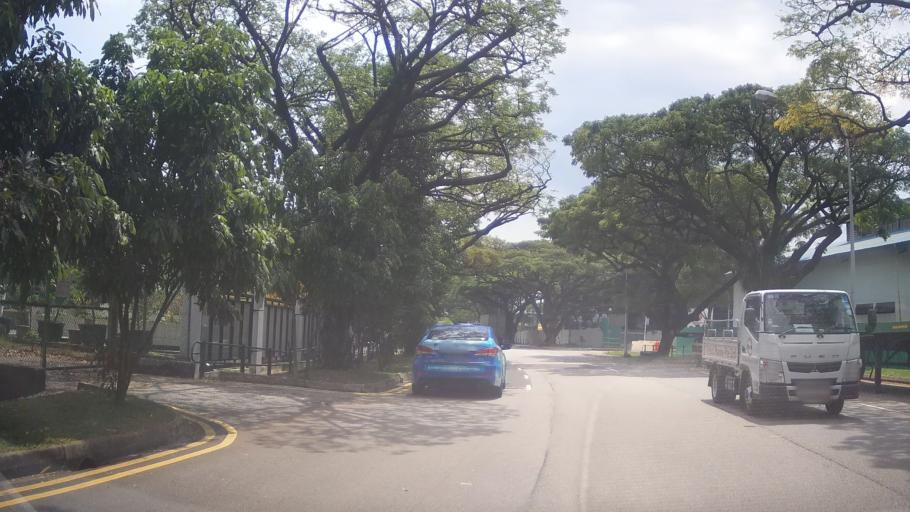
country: MY
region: Johor
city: Johor Bahru
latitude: 1.3166
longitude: 103.6649
